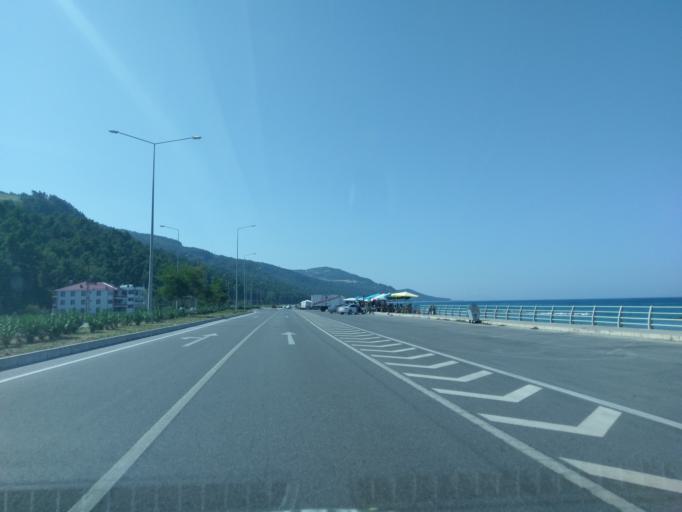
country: TR
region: Samsun
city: Yakakent
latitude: 41.6443
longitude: 35.4805
